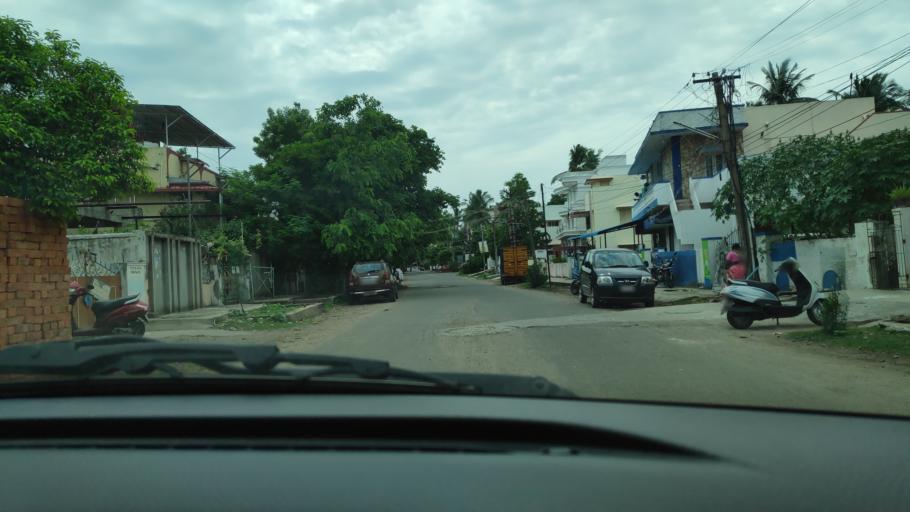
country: IN
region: Tamil Nadu
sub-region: Kancheepuram
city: Pallavaram
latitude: 12.9331
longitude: 80.1331
